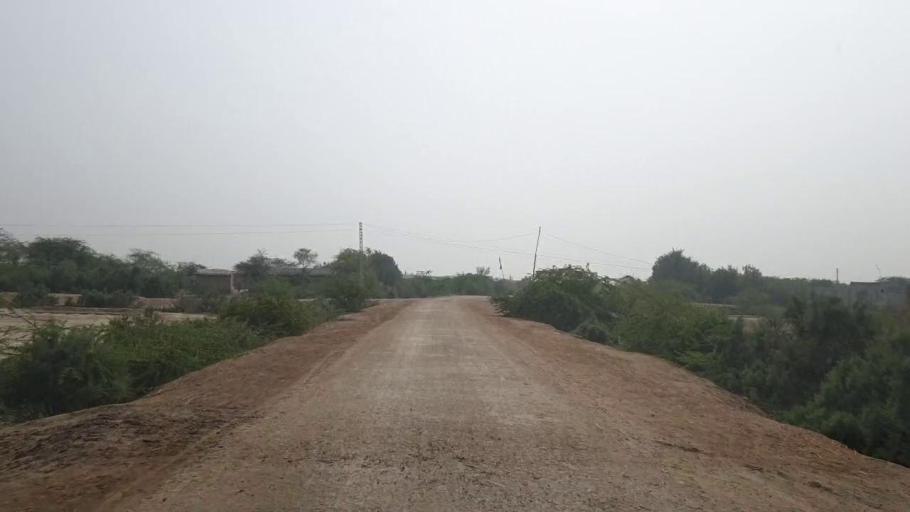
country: PK
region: Sindh
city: Kario
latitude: 24.6476
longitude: 68.6096
